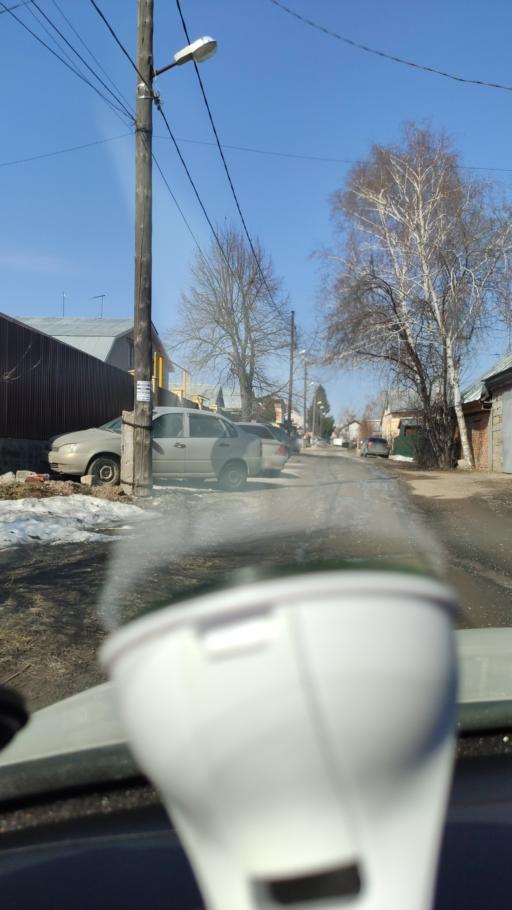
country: RU
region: Samara
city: Petra-Dubrava
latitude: 53.2903
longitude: 50.2810
